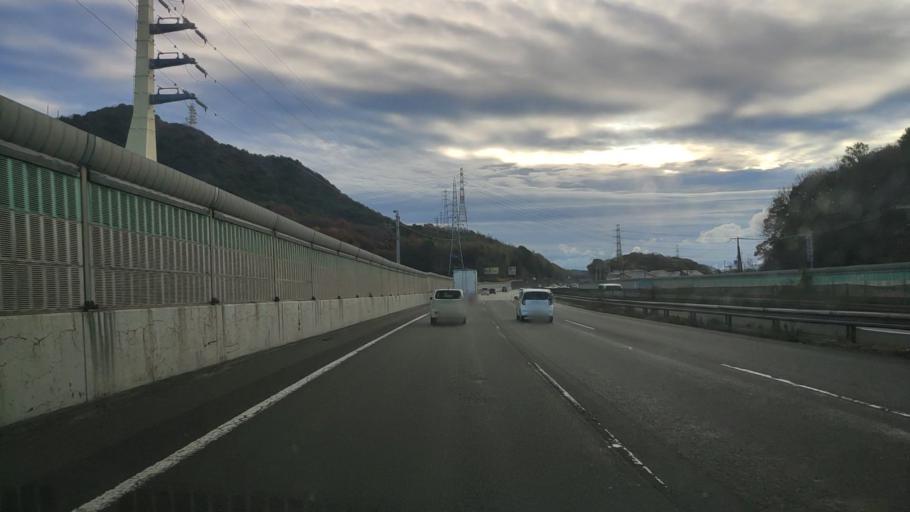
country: JP
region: Hyogo
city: Himeji
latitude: 34.8057
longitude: 134.7017
